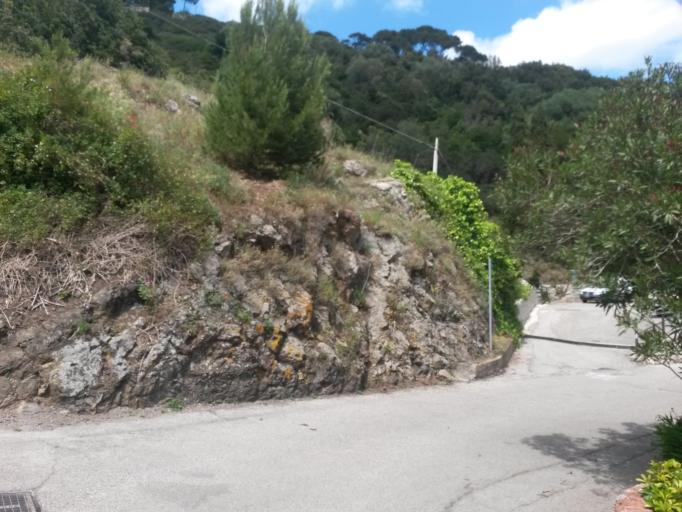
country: IT
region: Tuscany
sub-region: Provincia di Livorno
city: Rio nell'Elba
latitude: 42.8153
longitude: 10.3999
